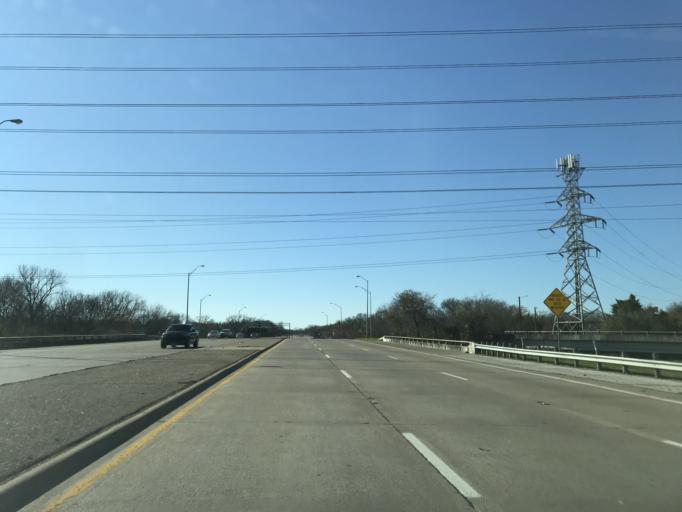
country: US
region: Texas
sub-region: Dallas County
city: Hutchins
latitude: 32.7005
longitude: -96.7545
